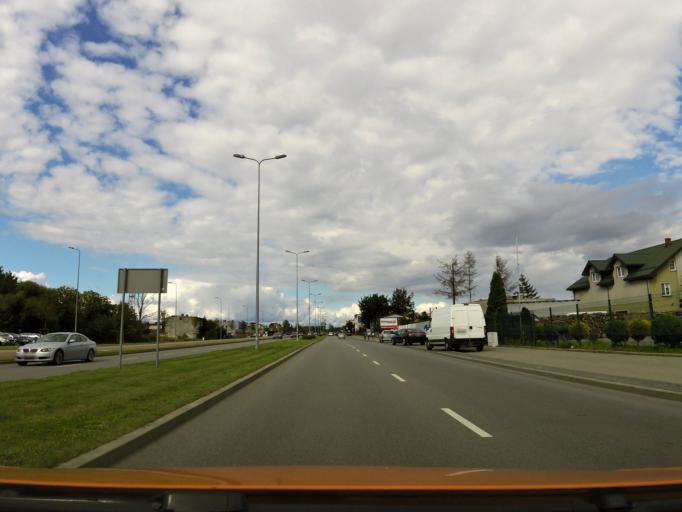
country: PL
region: West Pomeranian Voivodeship
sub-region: Powiat kolobrzeski
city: Kolobrzeg
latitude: 54.1694
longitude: 15.5546
